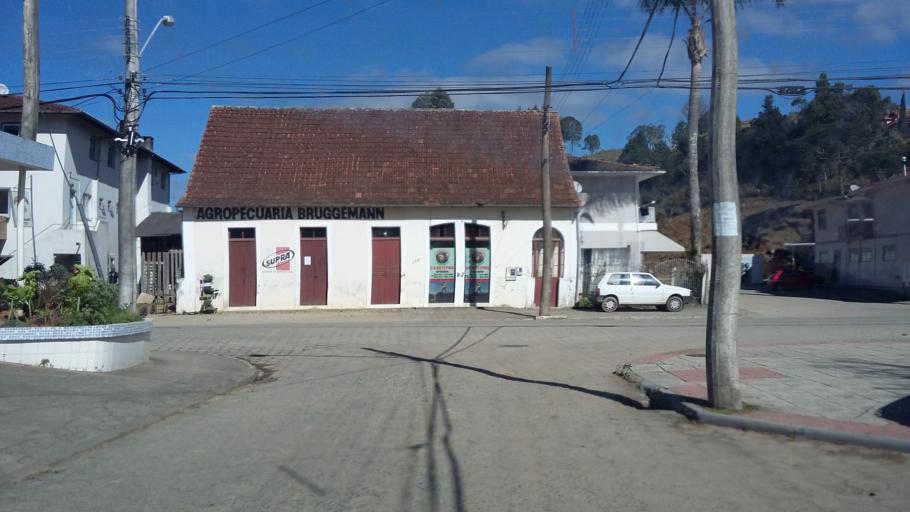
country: BR
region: Santa Catarina
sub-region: Santo Amaro Da Imperatriz
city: Santo Amaro da Imperatriz
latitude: -27.6734
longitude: -49.0123
